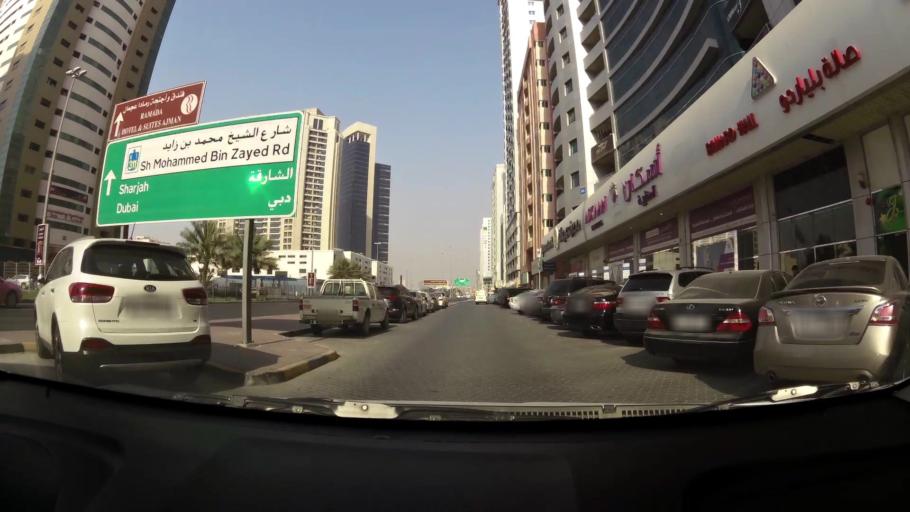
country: AE
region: Ajman
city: Ajman
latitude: 25.3921
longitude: 55.4362
